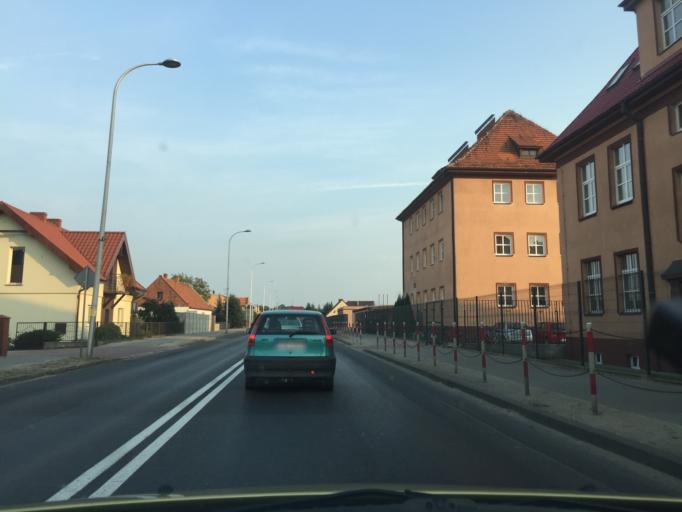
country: PL
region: Greater Poland Voivodeship
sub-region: Powiat jarocinski
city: Jarocin
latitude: 51.9621
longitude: 17.5123
